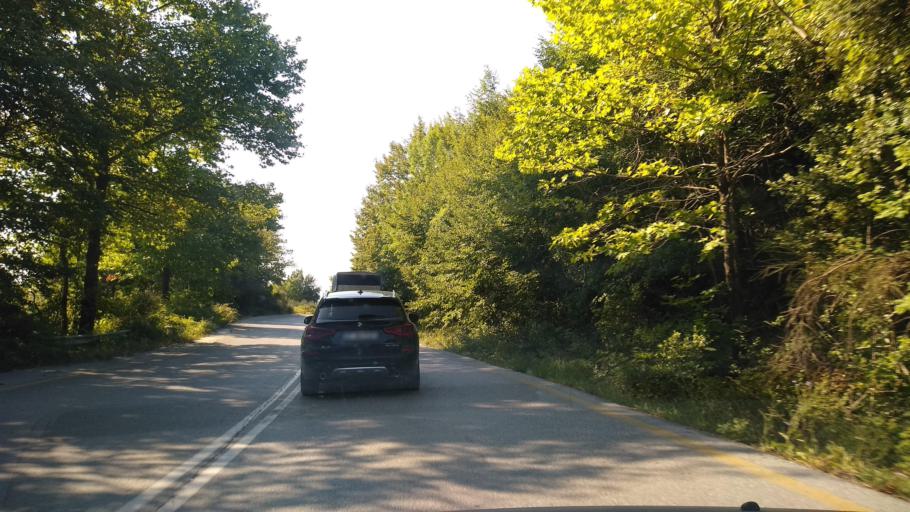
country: GR
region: Central Macedonia
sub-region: Nomos Chalkidikis
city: Stratonion
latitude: 40.5289
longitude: 23.8233
